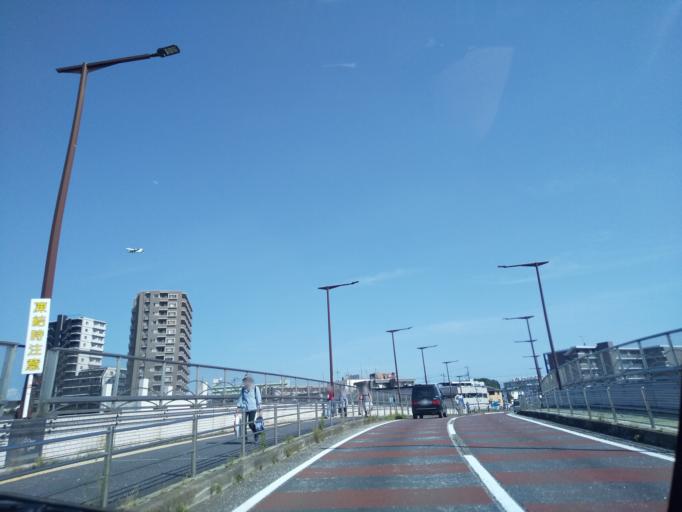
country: JP
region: Kanagawa
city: Zama
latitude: 35.4674
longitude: 139.4144
